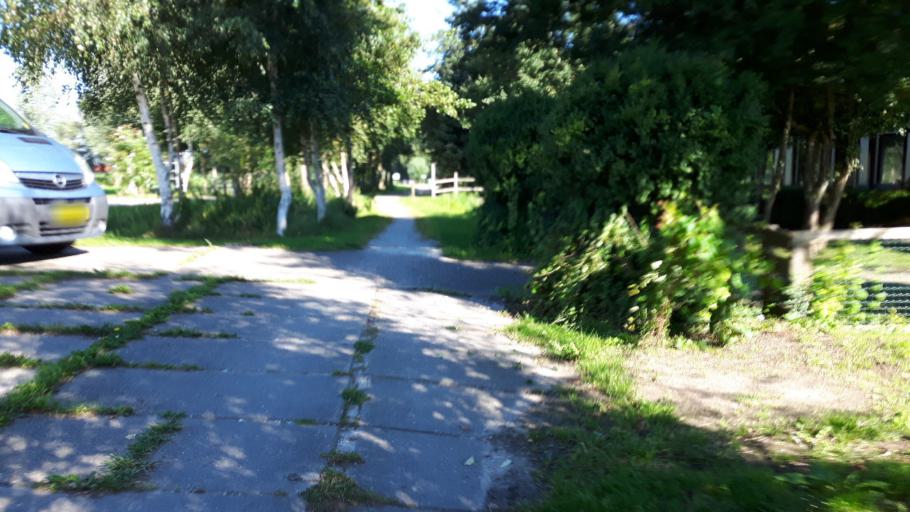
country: NL
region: Friesland
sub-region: Gemeente Lemsterland
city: Echtenerbrug
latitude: 52.8246
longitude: 5.8800
